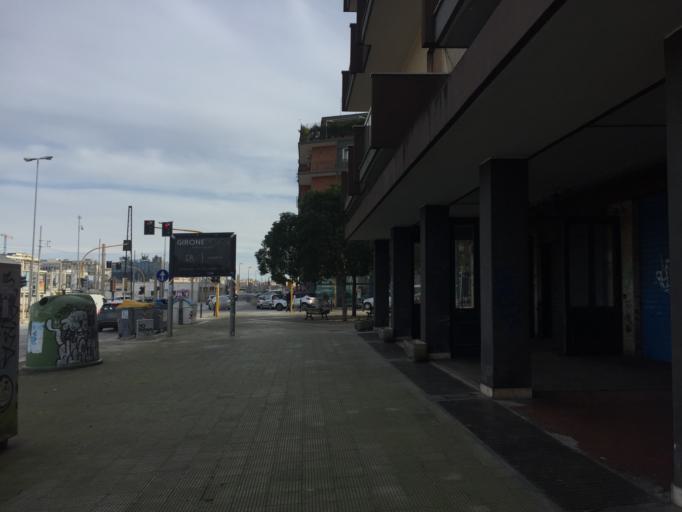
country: IT
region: Apulia
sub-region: Provincia di Bari
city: Bari
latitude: 41.1166
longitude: 16.8642
